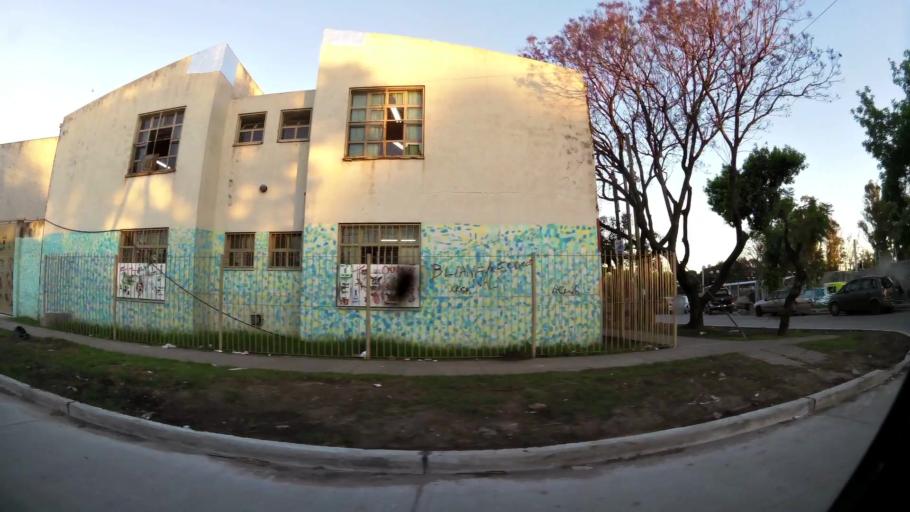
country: AR
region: Buenos Aires
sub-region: Partido de Almirante Brown
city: Adrogue
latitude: -34.8001
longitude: -58.3397
